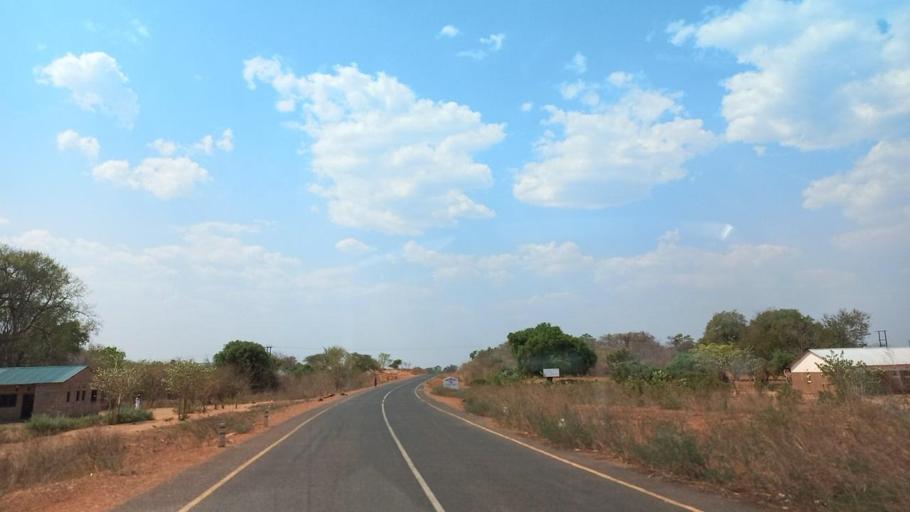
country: ZM
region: Lusaka
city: Luangwa
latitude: -15.4150
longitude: 30.3706
